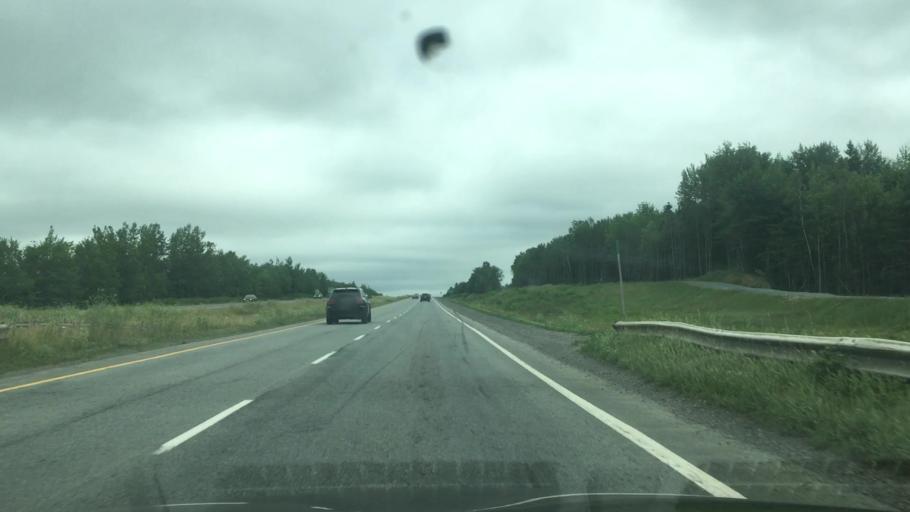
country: CA
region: Nova Scotia
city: Cole Harbour
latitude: 44.9848
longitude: -63.5016
